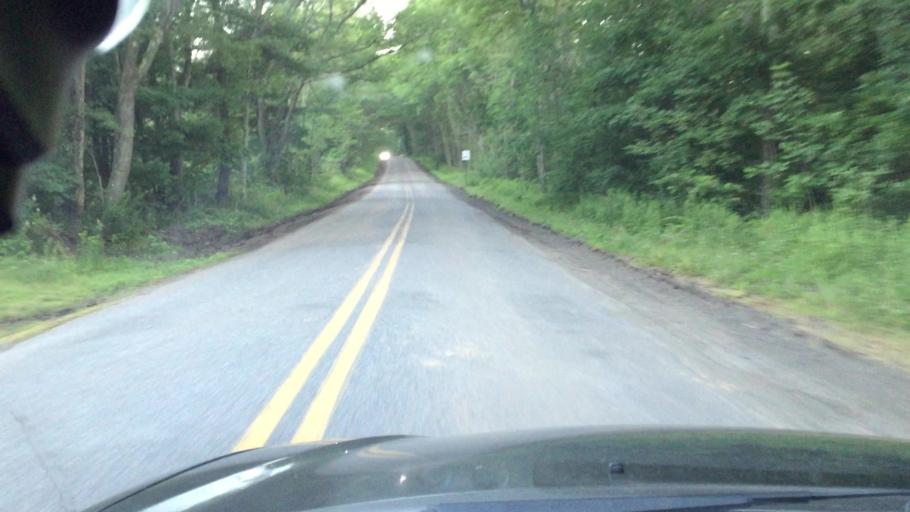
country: US
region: Pennsylvania
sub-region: Luzerne County
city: Harleigh
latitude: 41.0449
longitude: -75.9748
